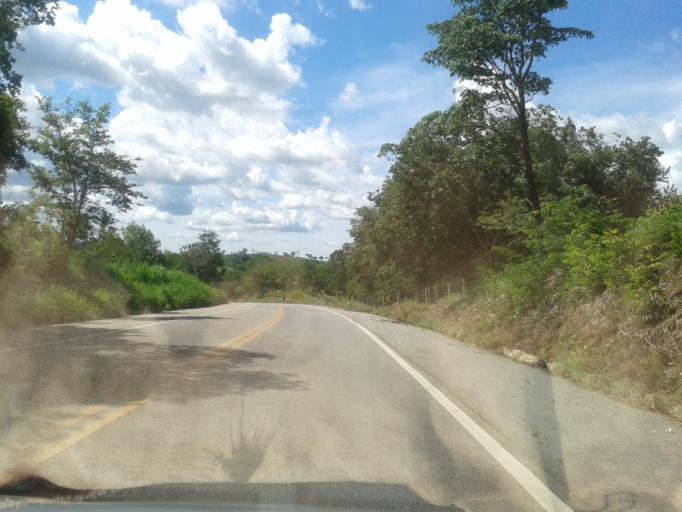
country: BR
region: Goias
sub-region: Itapuranga
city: Itapuranga
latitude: -15.6231
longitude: -50.2357
